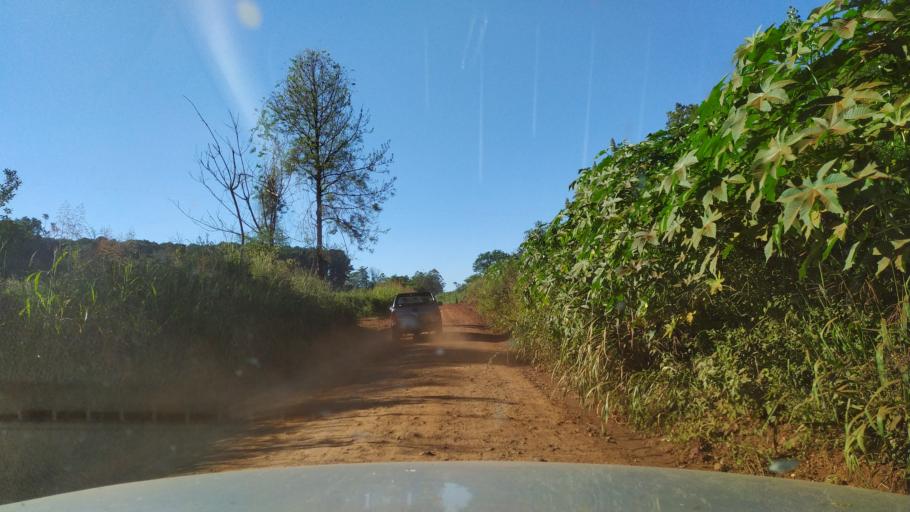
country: AR
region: Misiones
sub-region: Departamento de Montecarlo
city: Montecarlo
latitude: -26.6159
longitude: -54.6974
